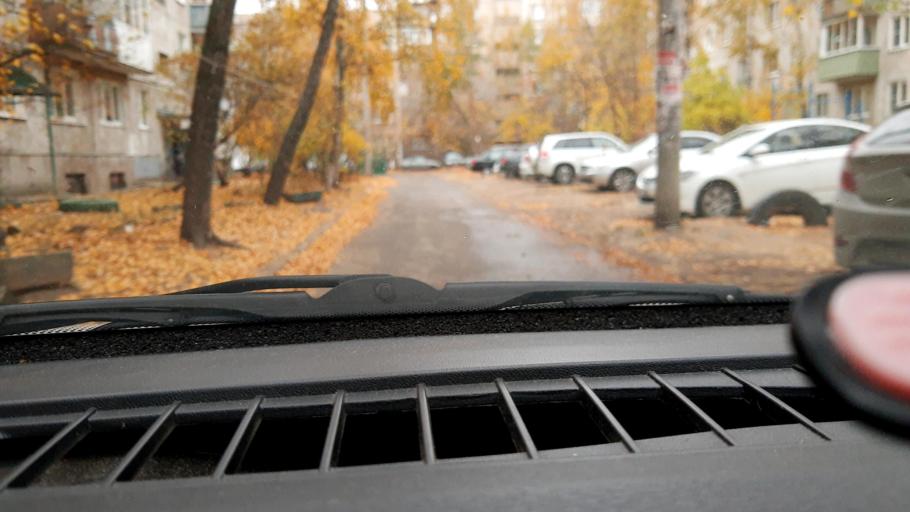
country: RU
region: Nizjnij Novgorod
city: Gorbatovka
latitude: 56.3604
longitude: 43.8100
